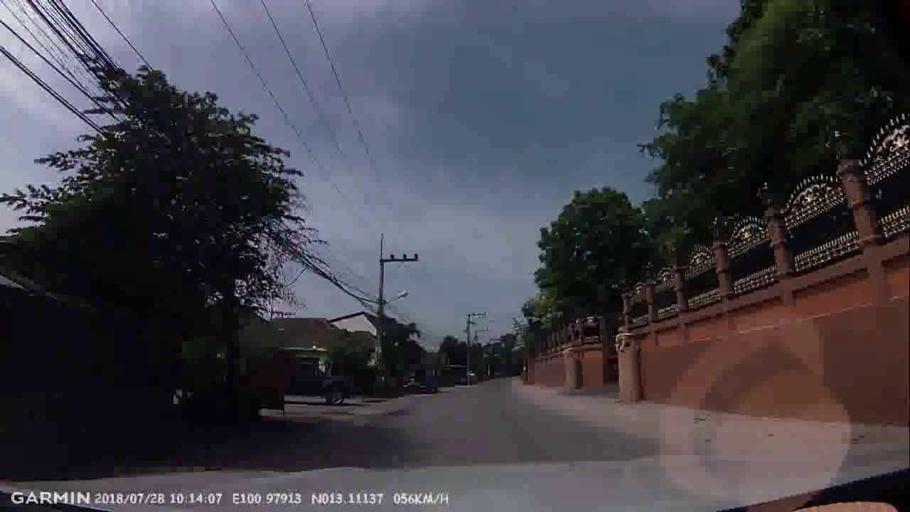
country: TH
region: Chon Buri
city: Ban Talat Bueng
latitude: 13.1112
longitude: 100.9791
